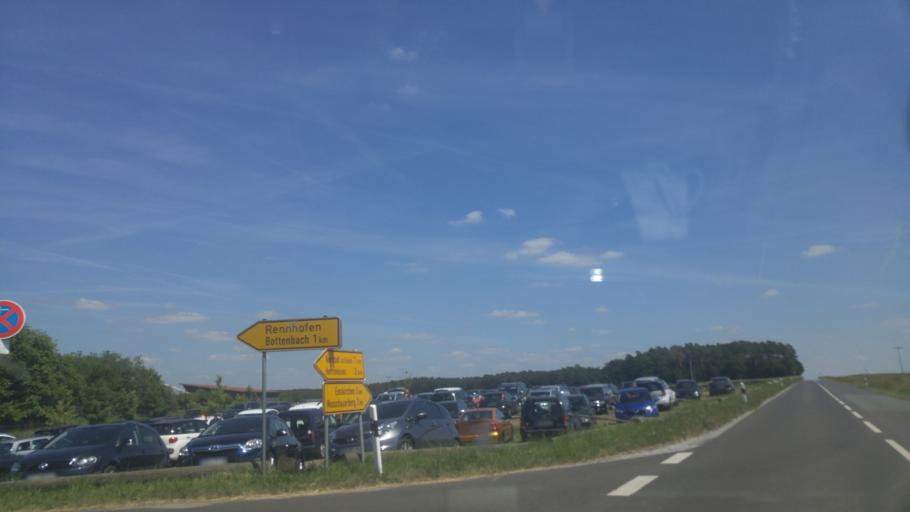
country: DE
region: Bavaria
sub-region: Regierungsbezirk Mittelfranken
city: Emskirchen
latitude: 49.5473
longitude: 10.6625
